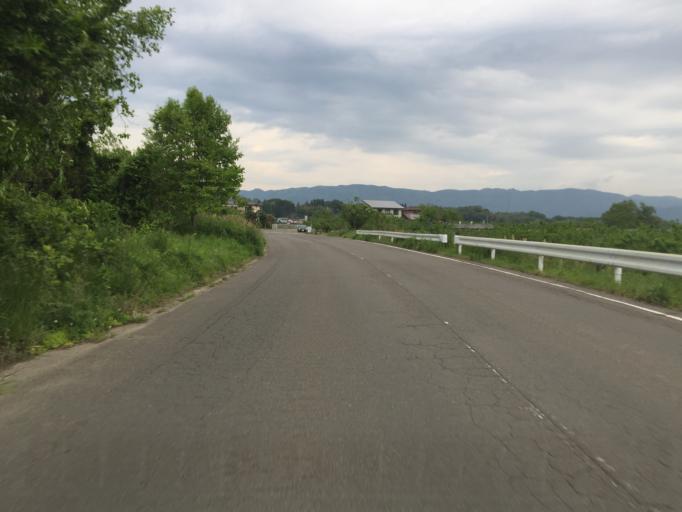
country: JP
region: Fukushima
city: Hobaramachi
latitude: 37.8429
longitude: 140.5375
